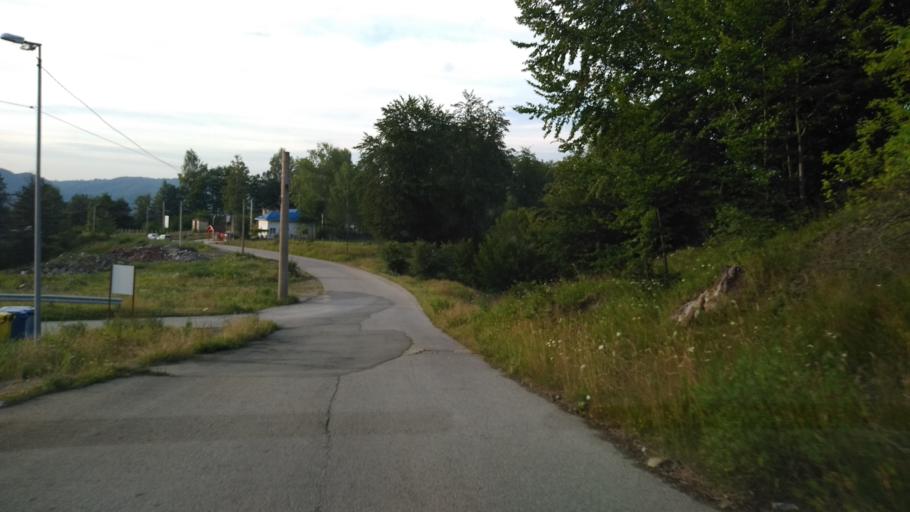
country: RO
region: Hunedoara
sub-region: Municipiul  Vulcan
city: Jiu-Paroseni
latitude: 45.3538
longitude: 23.2909
